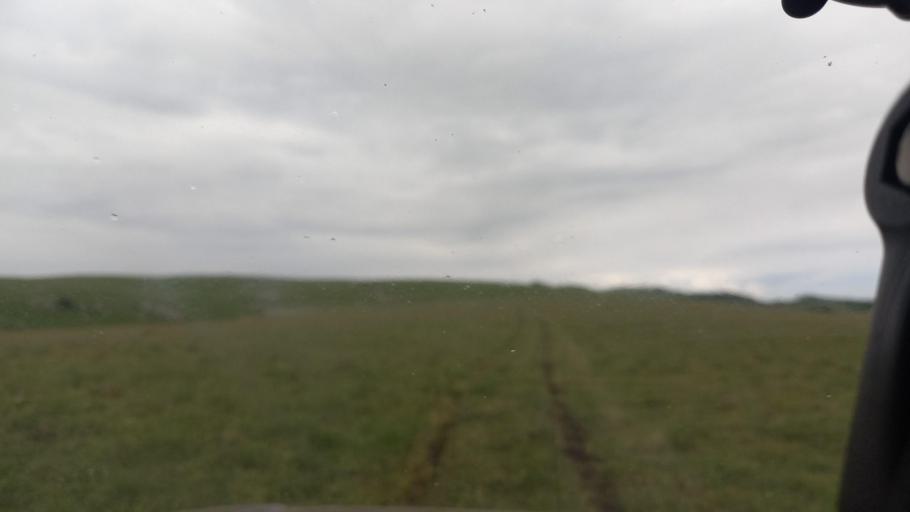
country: RU
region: Karachayevo-Cherkesiya
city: Pregradnaya
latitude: 43.9803
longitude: 41.3001
